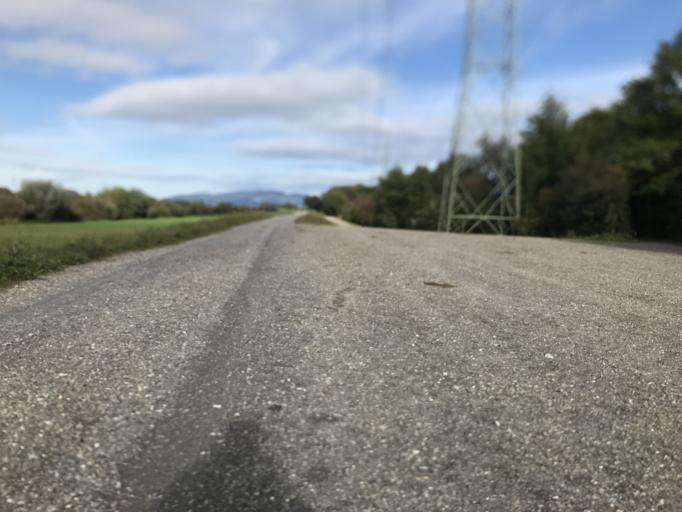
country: AT
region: Vorarlberg
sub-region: Politischer Bezirk Feldkirch
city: Mader
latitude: 47.3613
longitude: 9.6202
